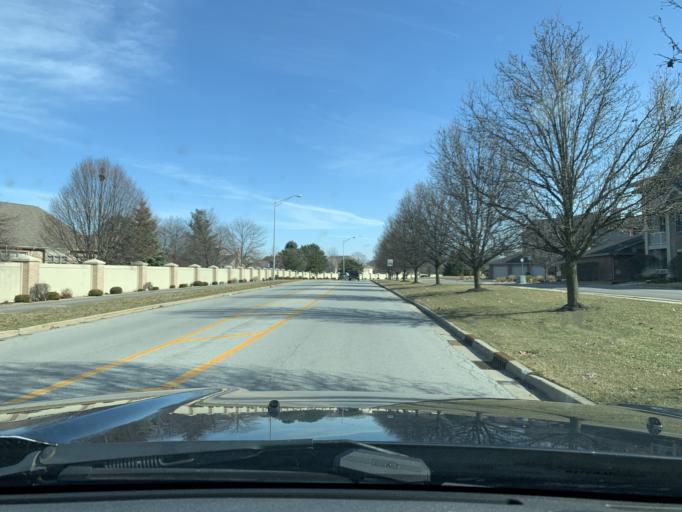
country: US
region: Indiana
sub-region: Lake County
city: Dyer
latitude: 41.5253
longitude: -87.4891
